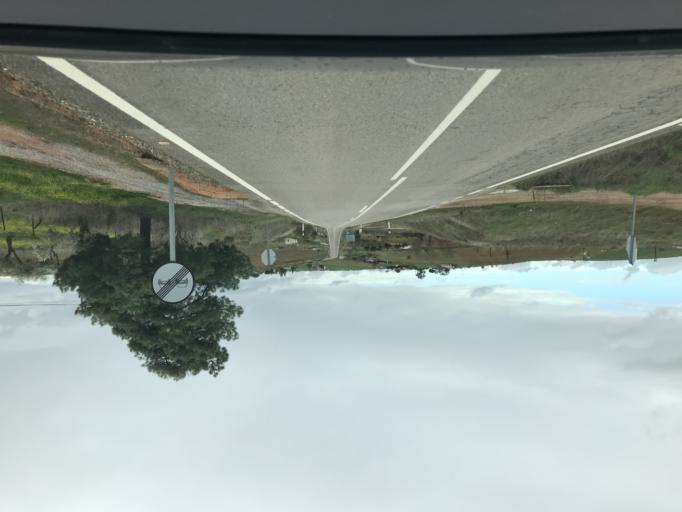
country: ES
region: Andalusia
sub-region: Province of Cordoba
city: Fuente Obejuna
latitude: 38.2504
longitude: -5.4298
